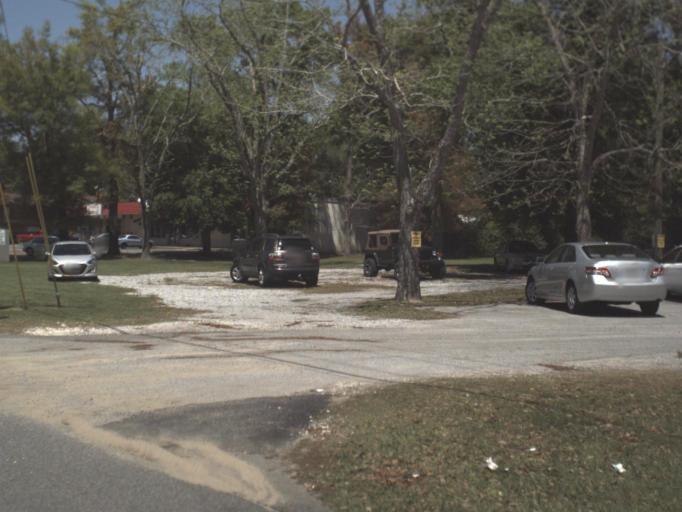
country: US
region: Florida
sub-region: Escambia County
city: Ferry Pass
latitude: 30.4973
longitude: -87.1710
